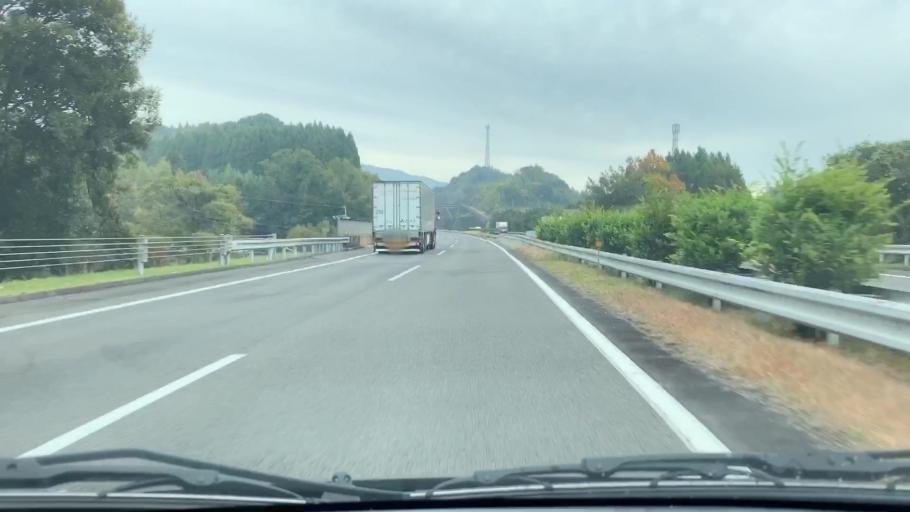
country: JP
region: Saga Prefecture
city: Takeocho-takeo
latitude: 33.2758
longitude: 130.1142
